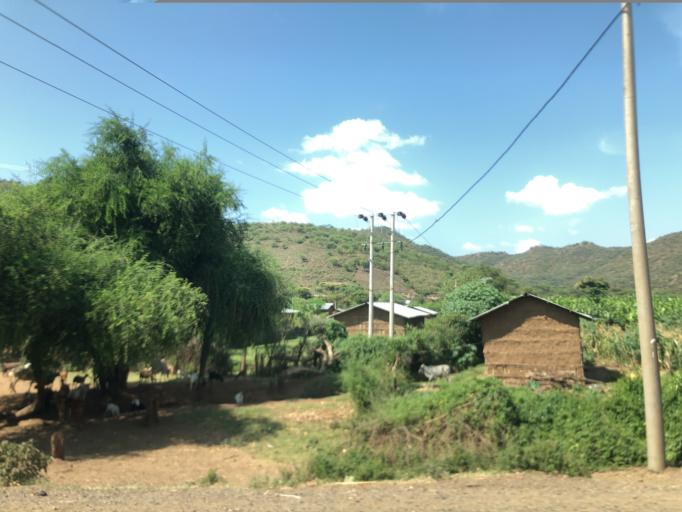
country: ET
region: Southern Nations, Nationalities, and People's Region
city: Gidole
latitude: 5.8217
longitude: 37.4557
